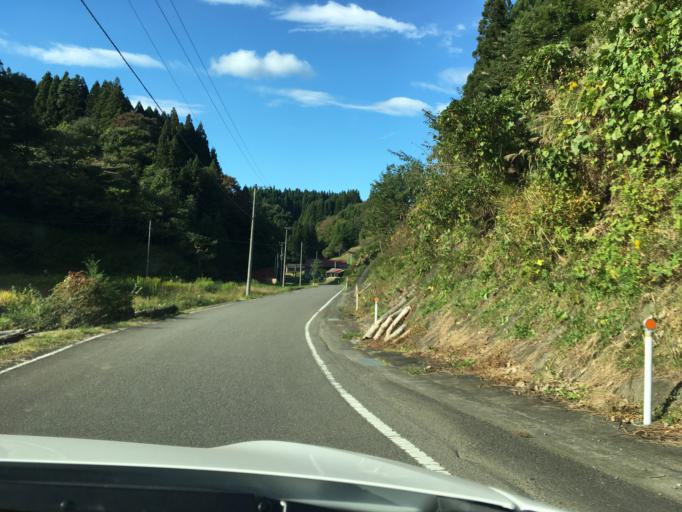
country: JP
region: Fukushima
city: Ishikawa
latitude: 37.1462
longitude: 140.5406
